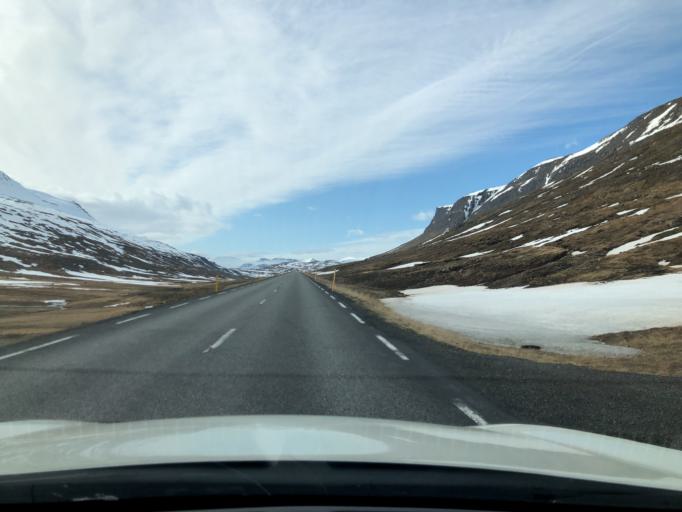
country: IS
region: East
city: Reydarfjoerdur
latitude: 65.1268
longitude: -14.3342
